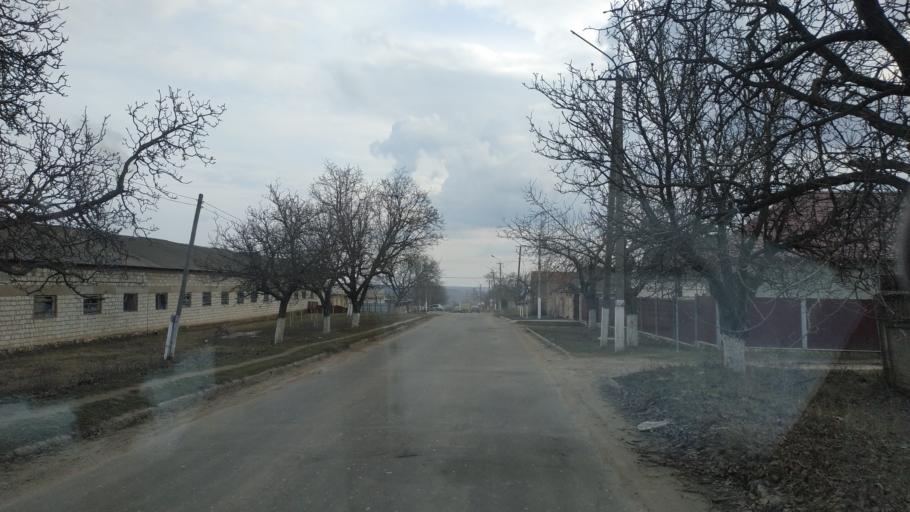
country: MD
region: Anenii Noi
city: Varnita
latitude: 46.8517
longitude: 29.3517
